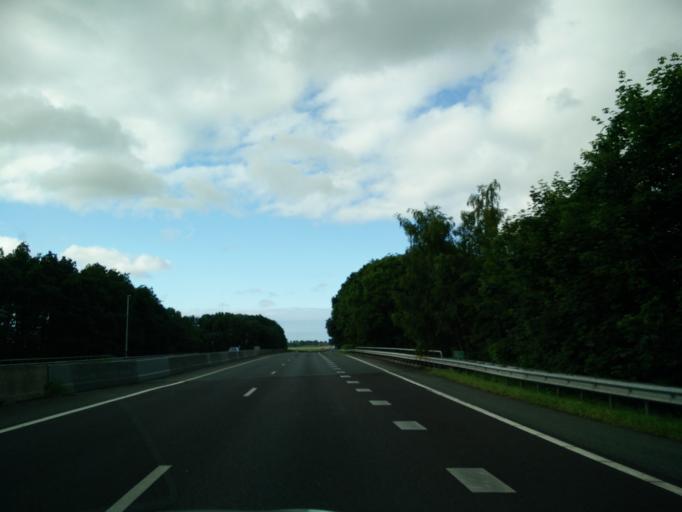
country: NL
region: Groningen
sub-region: Gemeente Haren
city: Haren
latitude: 53.1270
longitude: 6.6100
